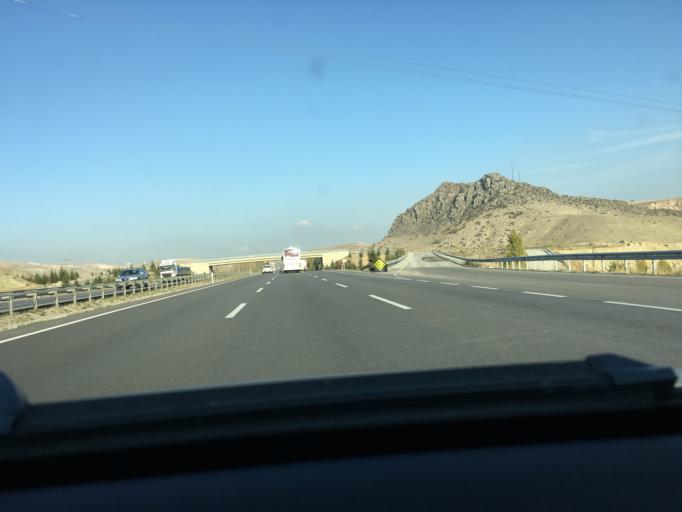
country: TR
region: Ankara
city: Temelli
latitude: 39.7688
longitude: 32.4870
